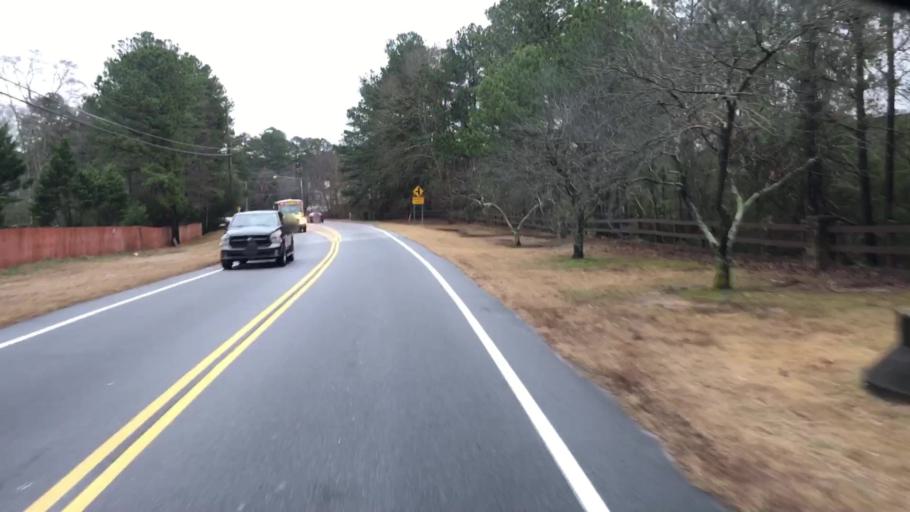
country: US
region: Georgia
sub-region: Gwinnett County
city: Snellville
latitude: 33.8238
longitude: -83.9778
